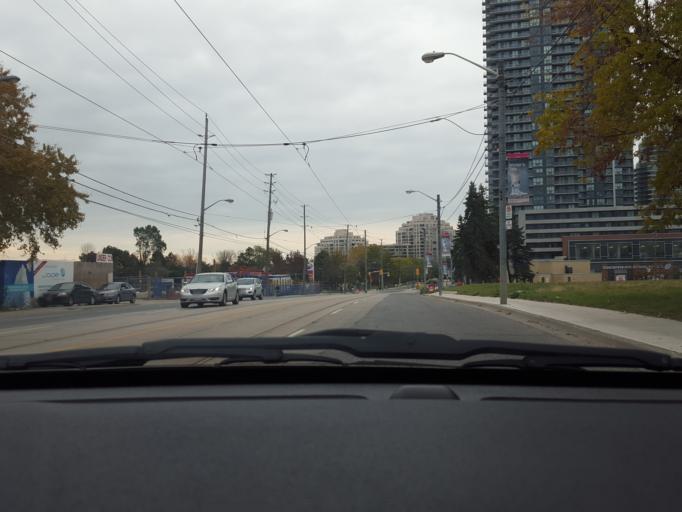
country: CA
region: Ontario
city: Etobicoke
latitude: 43.6248
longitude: -79.4803
